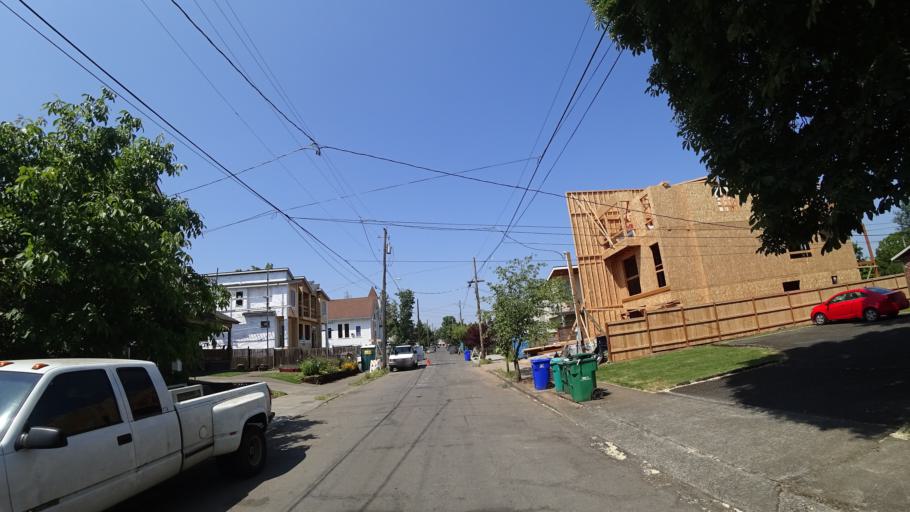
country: US
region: Oregon
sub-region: Multnomah County
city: Portland
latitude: 45.5641
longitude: -122.6571
